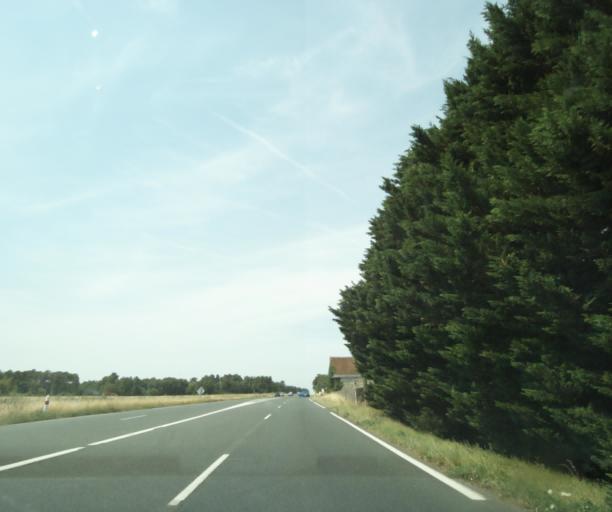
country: FR
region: Centre
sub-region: Departement d'Indre-et-Loire
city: La Celle-Saint-Avant
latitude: 47.0599
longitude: 0.6160
